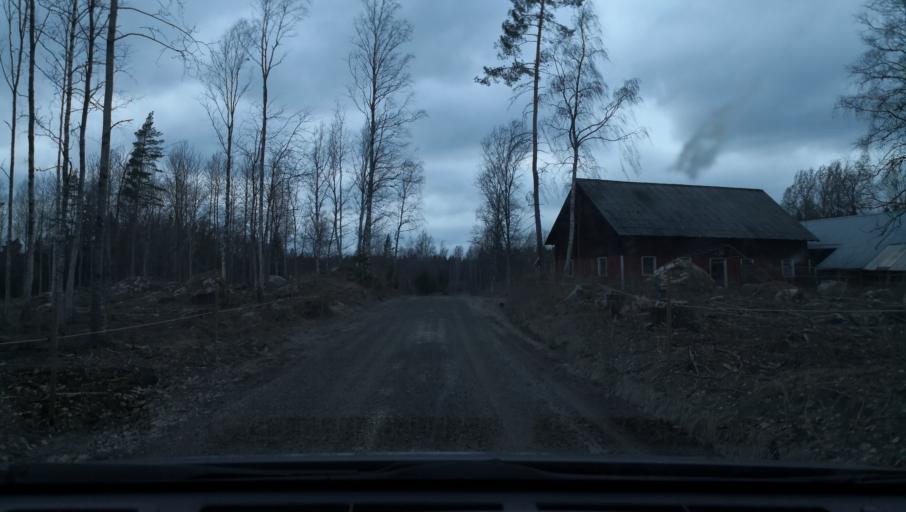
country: SE
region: OErebro
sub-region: Lindesbergs Kommun
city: Fellingsbro
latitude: 59.5993
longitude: 15.6225
